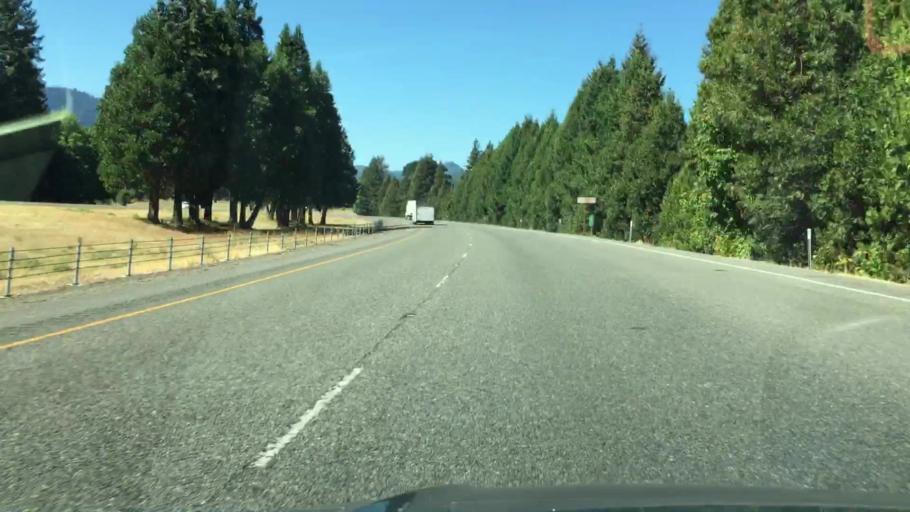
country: US
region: Oregon
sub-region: Douglas County
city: Canyonville
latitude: 42.7672
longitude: -123.3253
